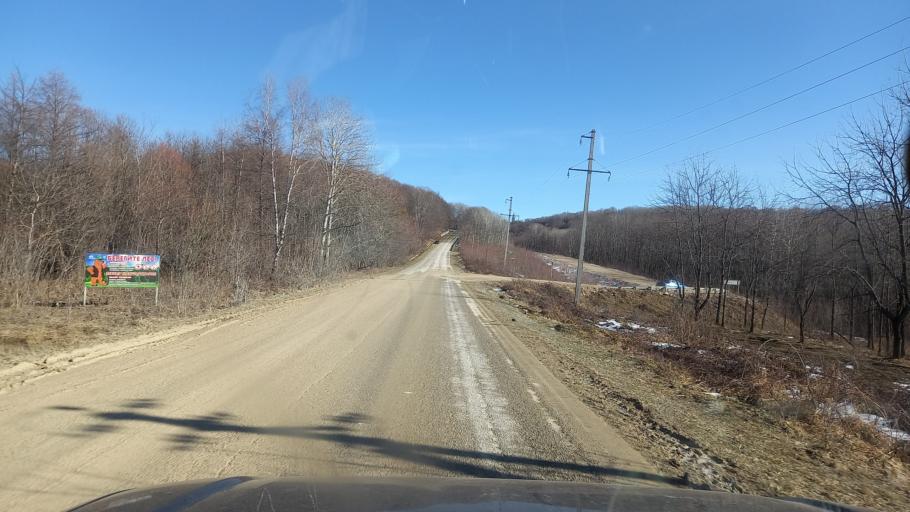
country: RU
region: Adygeya
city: Kamennomostskiy
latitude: 44.2867
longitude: 40.2997
